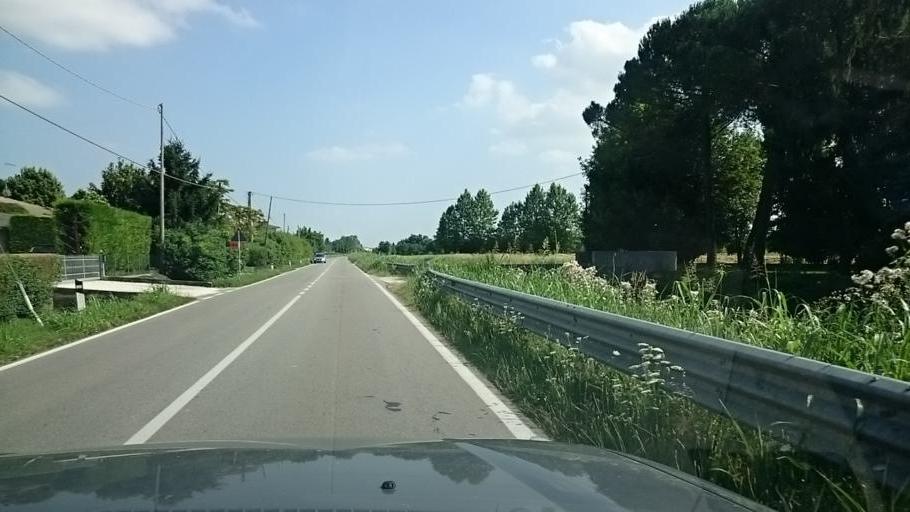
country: IT
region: Veneto
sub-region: Provincia di Padova
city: San Giorgio delle Pertiche
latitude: 45.5537
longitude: 11.8718
